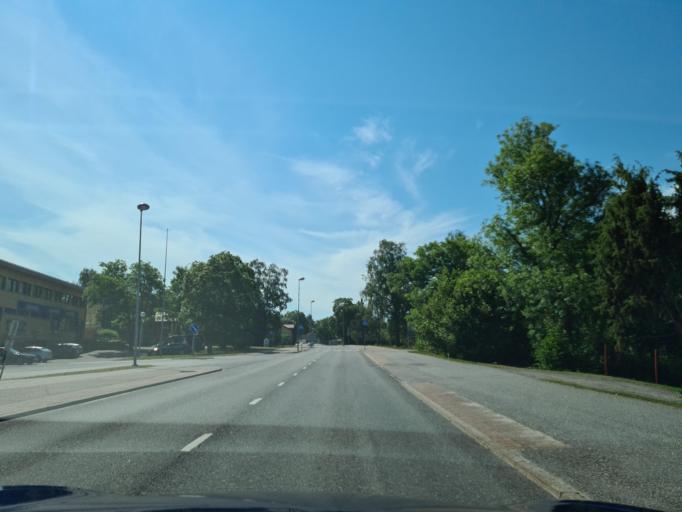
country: FI
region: Varsinais-Suomi
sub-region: Turku
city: Paimio
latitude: 60.4534
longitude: 22.6928
